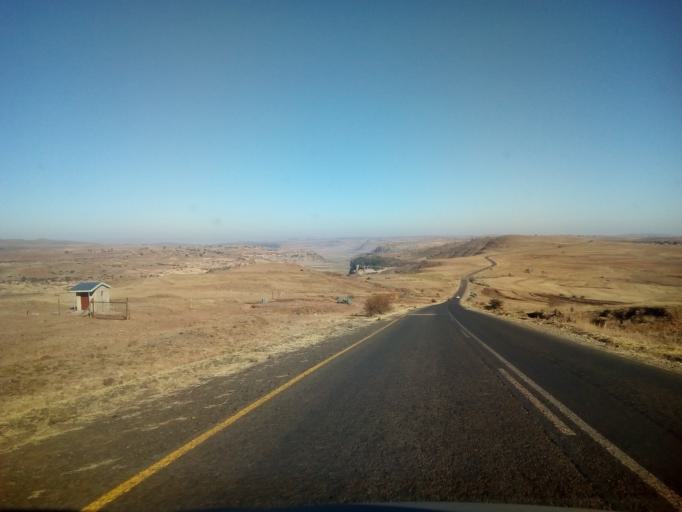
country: LS
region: Berea
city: Teyateyaneng
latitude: -29.2530
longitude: 27.7878
